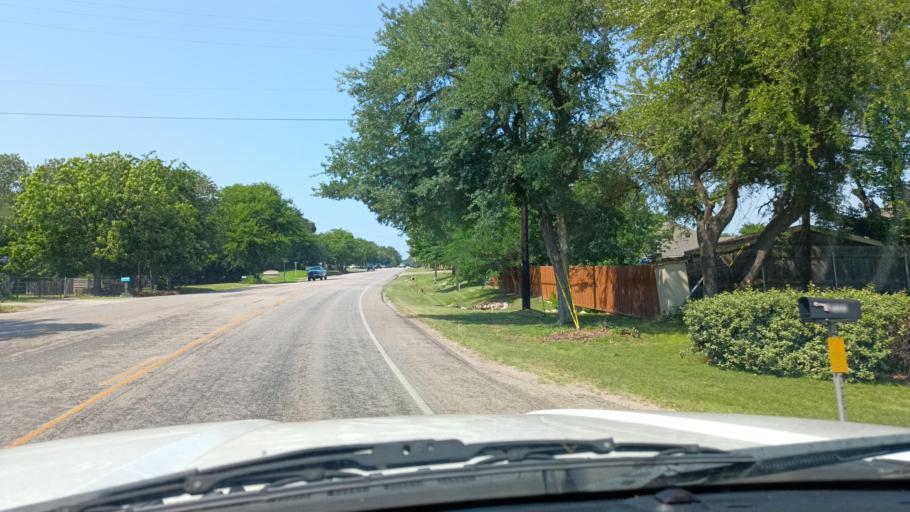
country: US
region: Texas
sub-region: Bell County
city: Morgans Point Resort
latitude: 31.1216
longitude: -97.4711
